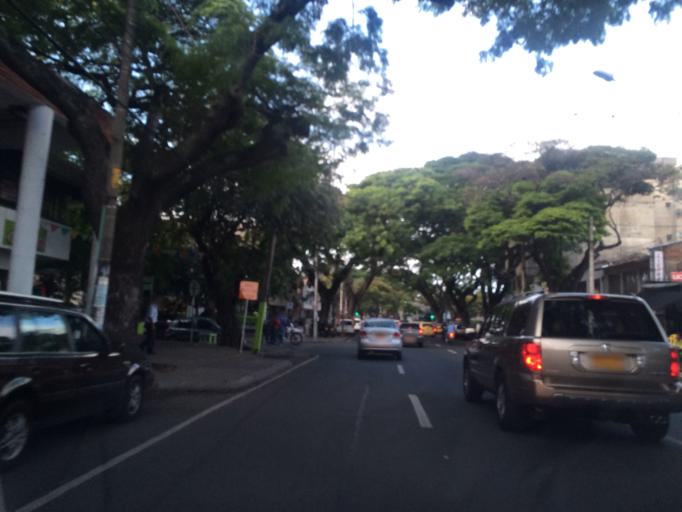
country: CO
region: Valle del Cauca
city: Cali
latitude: 3.4684
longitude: -76.5291
